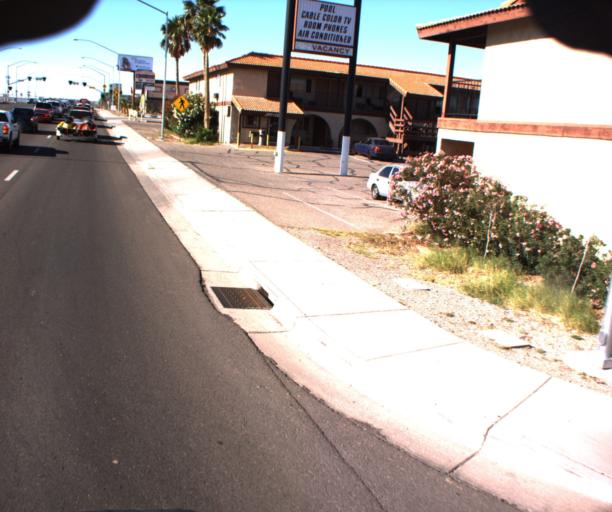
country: US
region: Arizona
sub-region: Mohave County
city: Bullhead City
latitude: 35.1513
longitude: -114.5679
